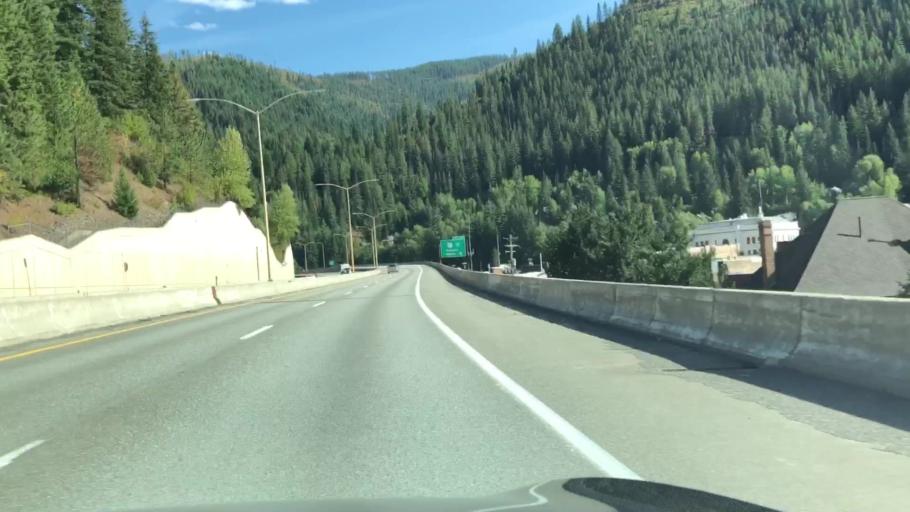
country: US
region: Idaho
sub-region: Shoshone County
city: Wallace
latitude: 47.4738
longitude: -115.9237
